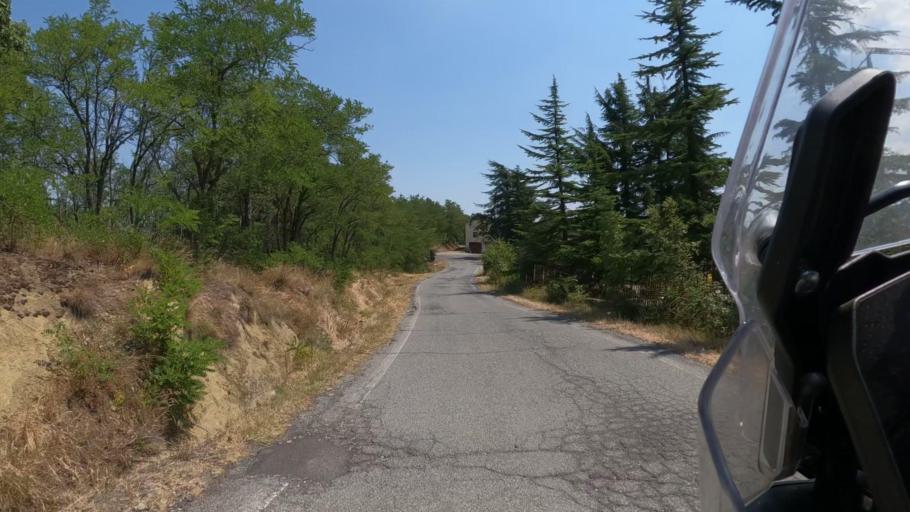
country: IT
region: Piedmont
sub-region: Provincia di Alessandria
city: Cassinelle-Concentrico
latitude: 44.5792
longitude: 8.5375
